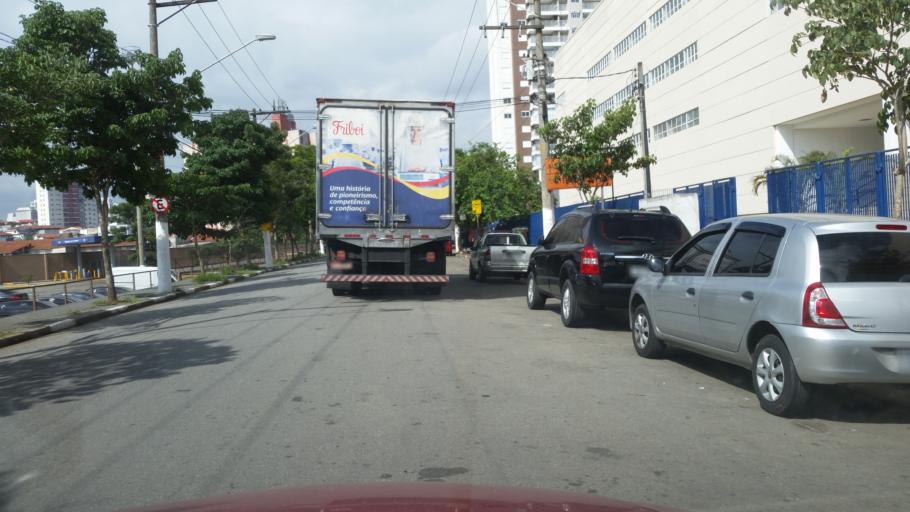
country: BR
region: Sao Paulo
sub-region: Diadema
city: Diadema
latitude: -23.6616
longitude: -46.7086
